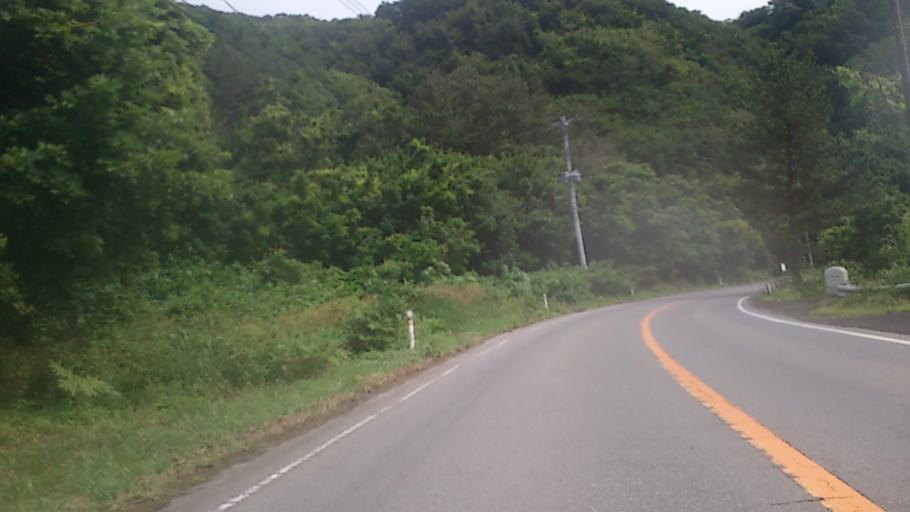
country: JP
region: Akita
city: Noshiromachi
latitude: 40.4503
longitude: 139.9430
